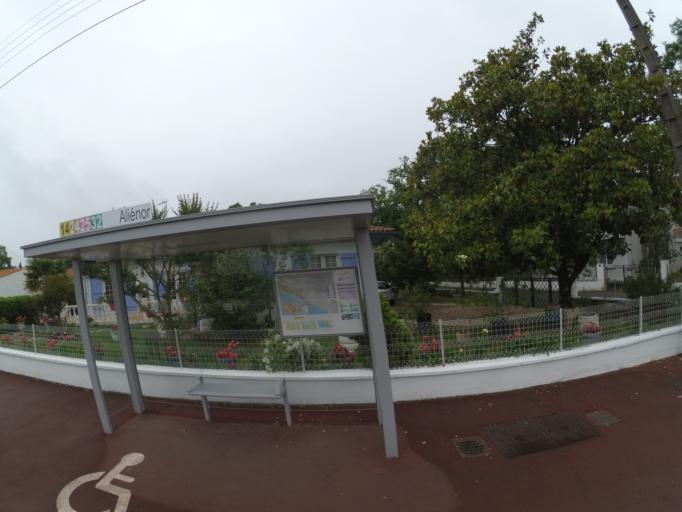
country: FR
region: Poitou-Charentes
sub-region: Departement de la Charente-Maritime
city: Saint-Georges-de-Didonne
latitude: 45.6166
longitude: -1.0030
